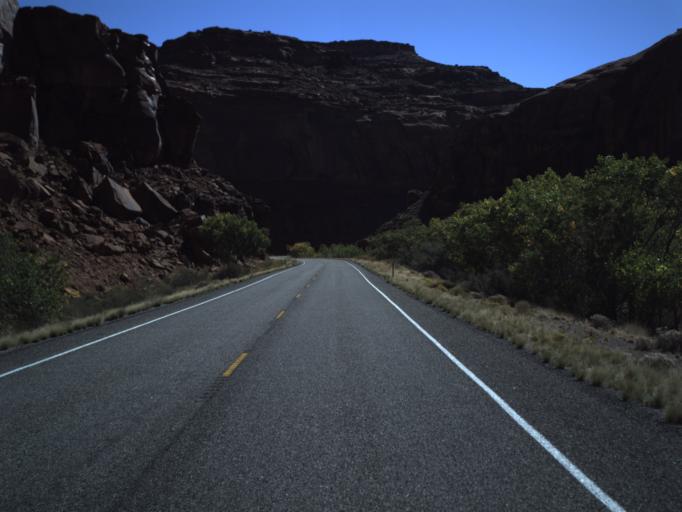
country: US
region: Utah
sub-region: San Juan County
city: Blanding
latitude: 37.9613
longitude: -110.4866
